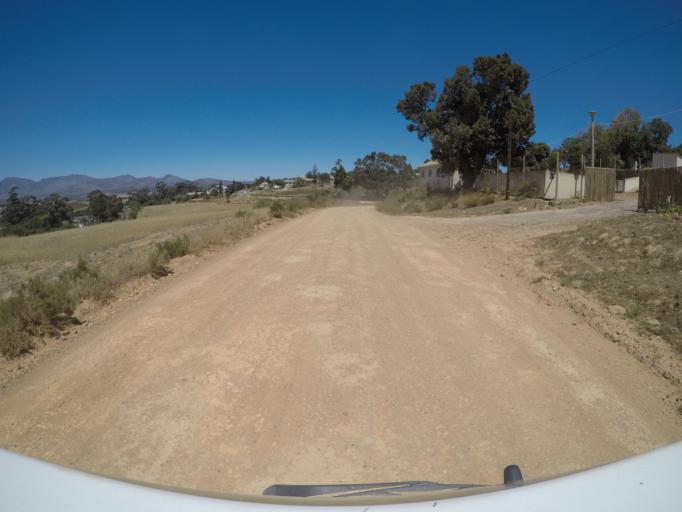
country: ZA
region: Western Cape
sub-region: Overberg District Municipality
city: Hermanus
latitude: -34.2217
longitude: 19.2053
